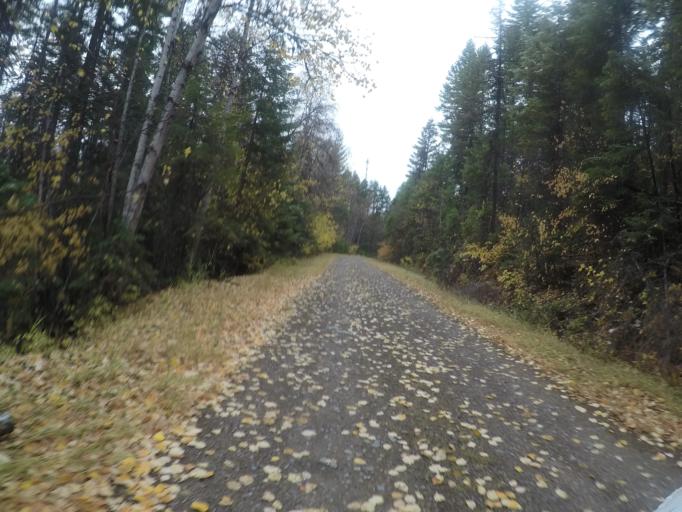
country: US
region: Montana
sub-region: Flathead County
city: Bigfork
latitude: 47.8828
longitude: -113.8756
